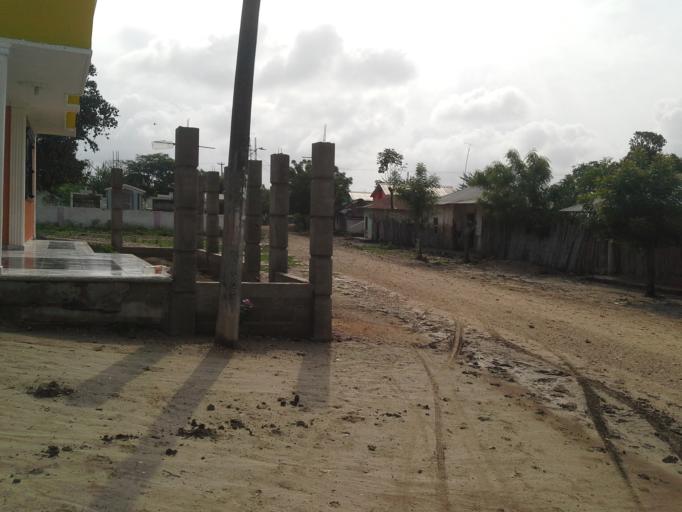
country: CO
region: Cordoba
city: Chima
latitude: 9.1029
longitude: -75.6247
